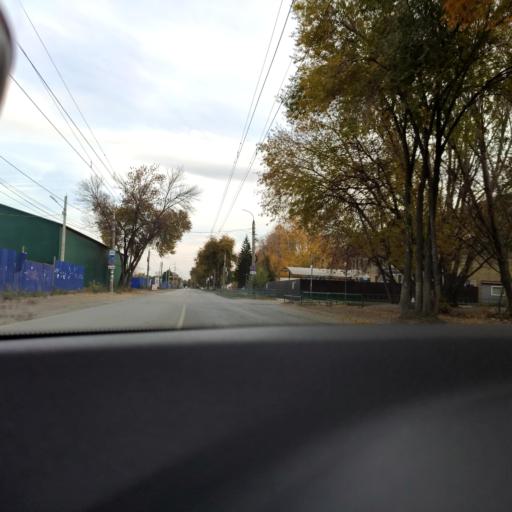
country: RU
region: Samara
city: Samara
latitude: 53.1971
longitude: 50.2701
